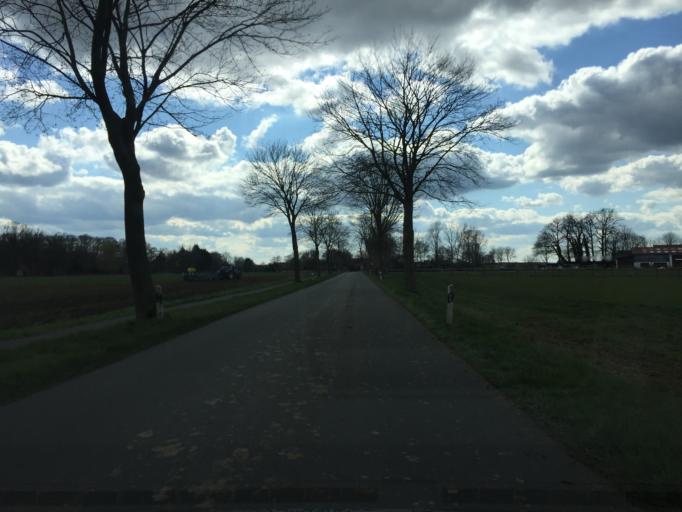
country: DE
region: Lower Saxony
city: Engeln
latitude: 52.7961
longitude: 8.9594
